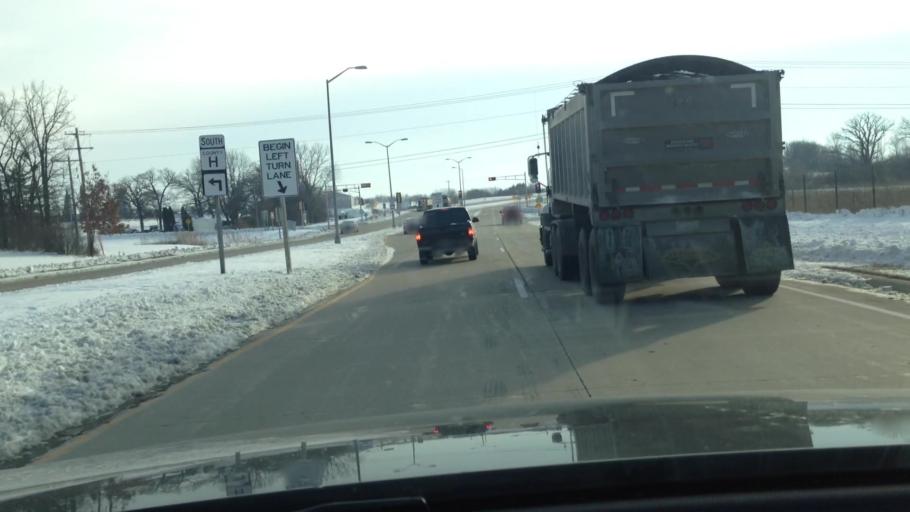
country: US
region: Wisconsin
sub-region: Walworth County
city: Lake Geneva
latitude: 42.5660
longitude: -88.4138
